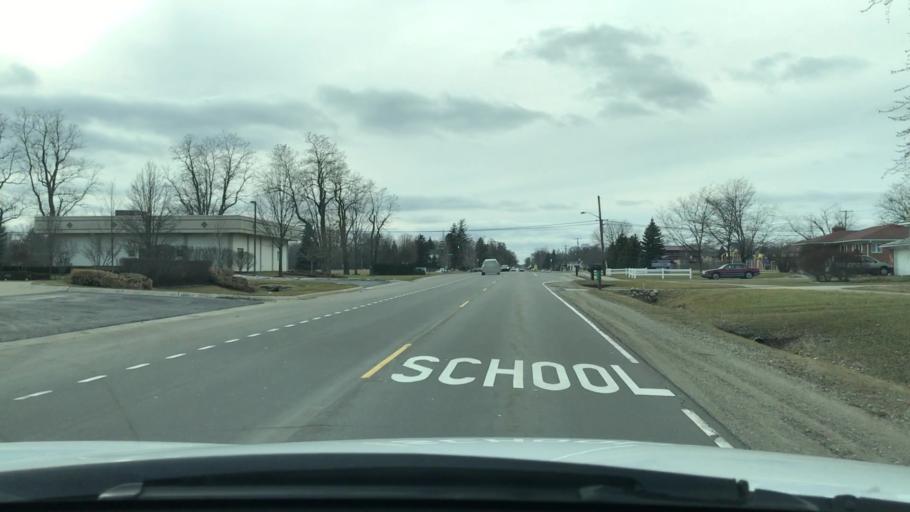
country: US
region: Michigan
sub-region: Oakland County
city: Waterford
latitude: 42.7197
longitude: -83.3578
